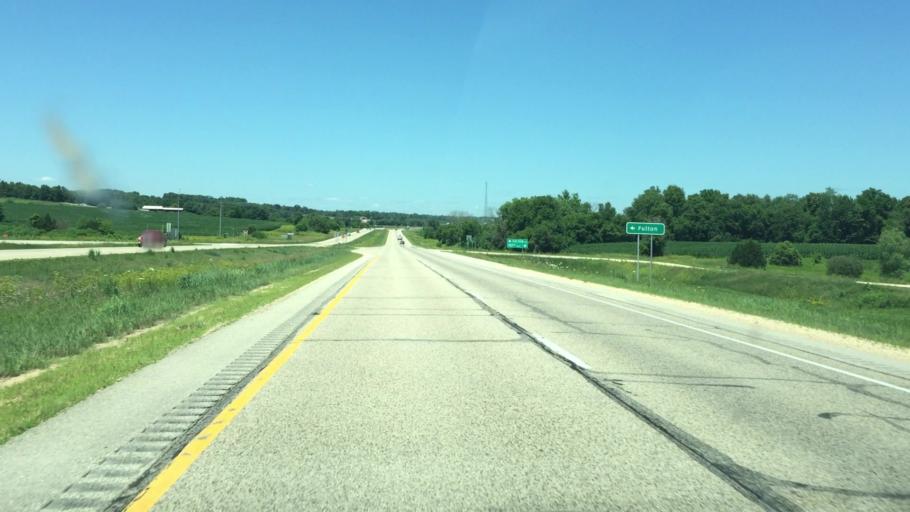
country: US
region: Iowa
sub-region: Jackson County
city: Maquoketa
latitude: 42.1543
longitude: -90.6761
